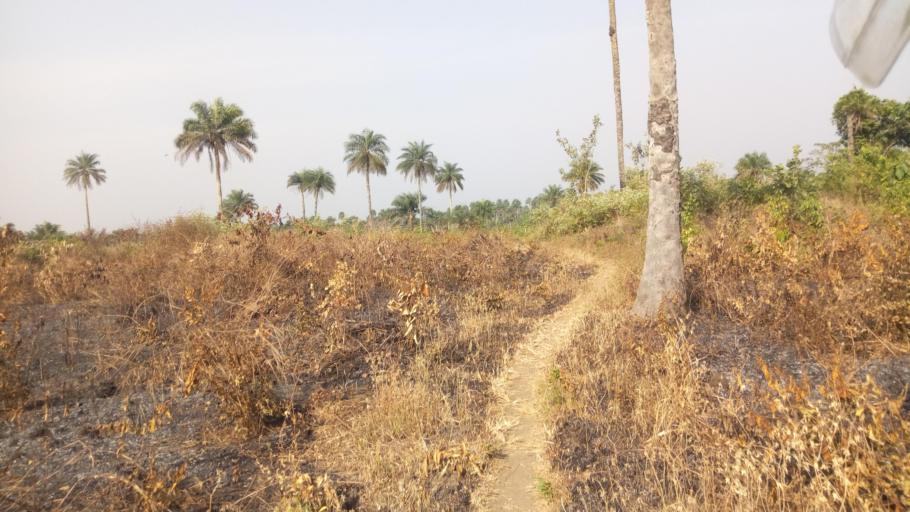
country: SL
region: Southern Province
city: Mogbwemo
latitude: 7.6155
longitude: -12.1728
